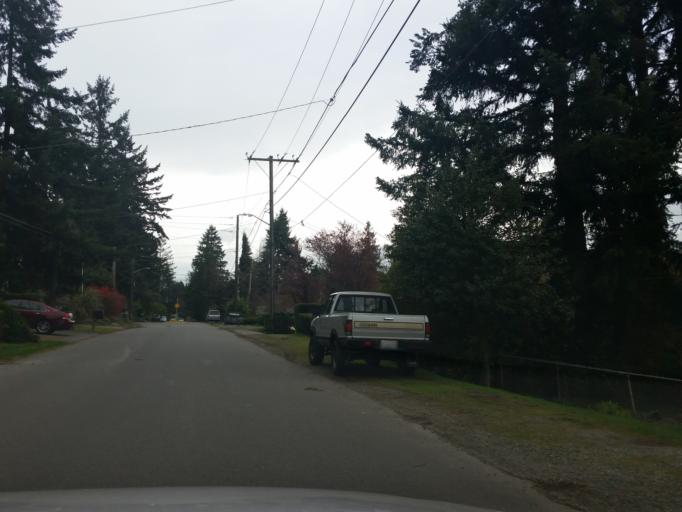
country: US
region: Washington
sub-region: King County
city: Shoreline
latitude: 47.7205
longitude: -122.3503
